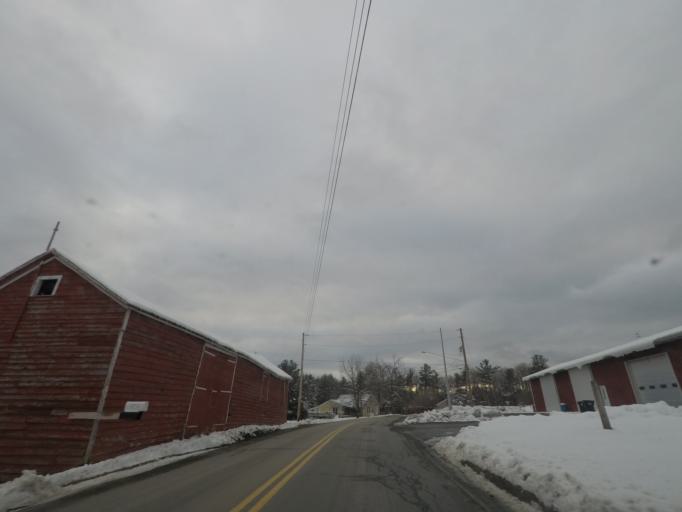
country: US
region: New York
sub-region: Rensselaer County
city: Averill Park
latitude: 42.6564
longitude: -73.5251
